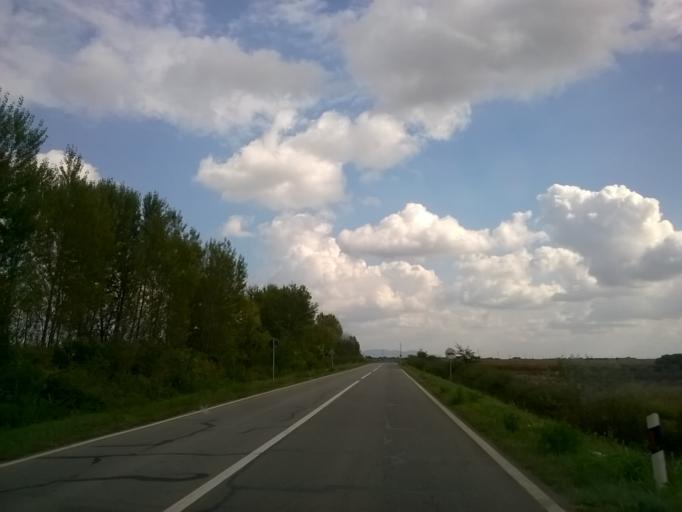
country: RS
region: Autonomna Pokrajina Vojvodina
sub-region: Juznobanatski Okrug
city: Plandiste
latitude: 45.2277
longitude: 21.1418
